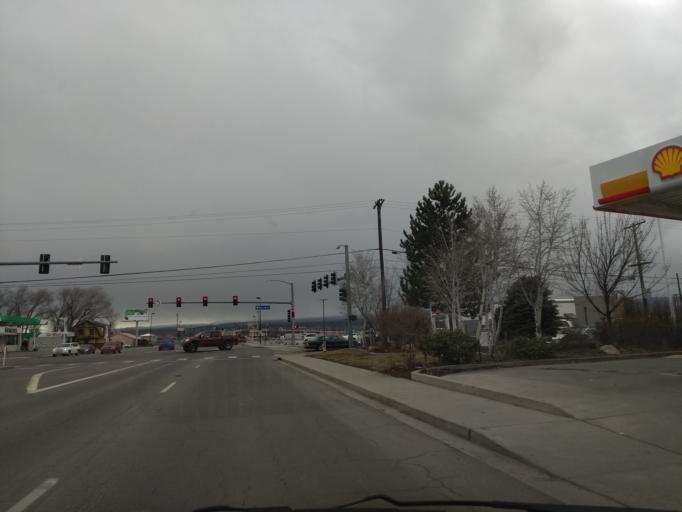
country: US
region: Colorado
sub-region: Mesa County
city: Fruitvale
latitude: 39.0778
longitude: -108.5153
